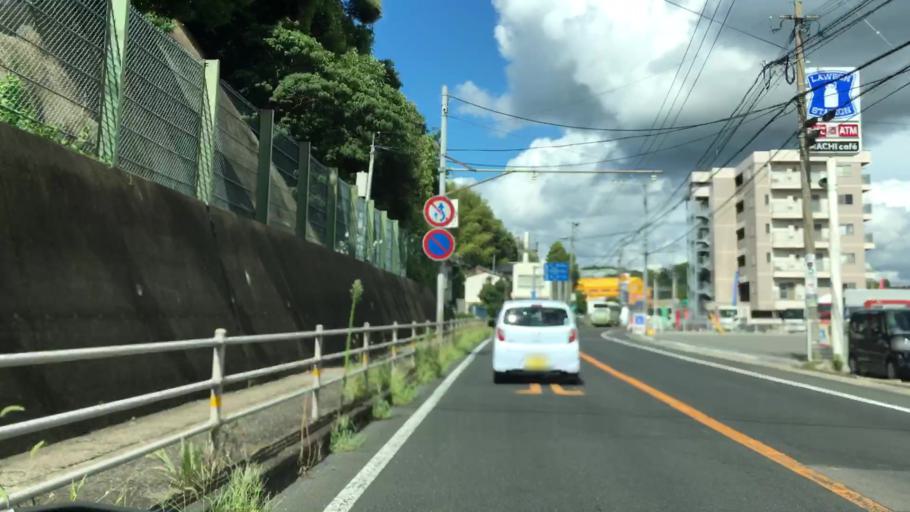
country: JP
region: Nagasaki
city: Sasebo
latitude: 33.1434
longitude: 129.8011
